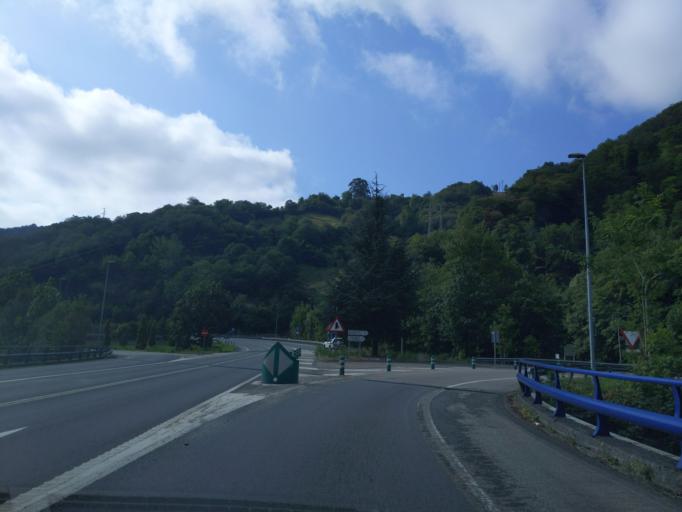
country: ES
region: Asturias
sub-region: Province of Asturias
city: El entrego
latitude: 43.2739
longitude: -5.6142
